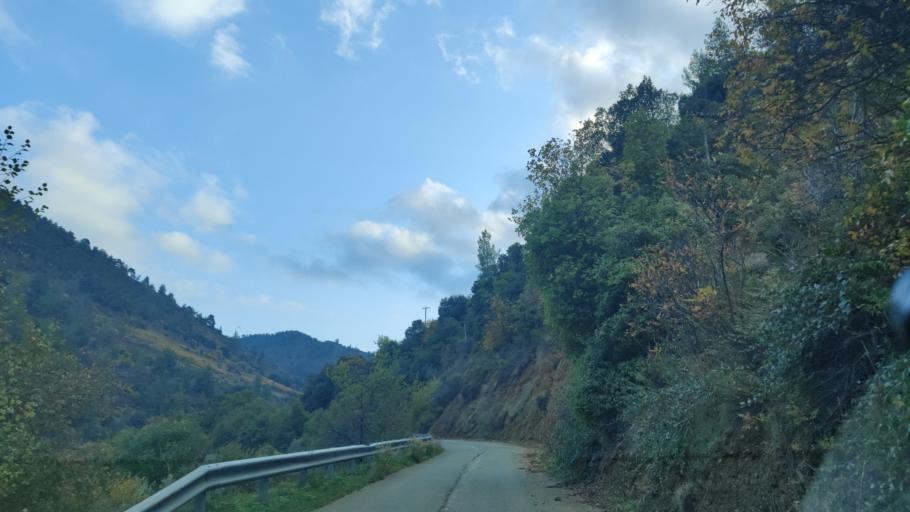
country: CY
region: Lefkosia
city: Lefka
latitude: 35.0504
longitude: 32.7354
